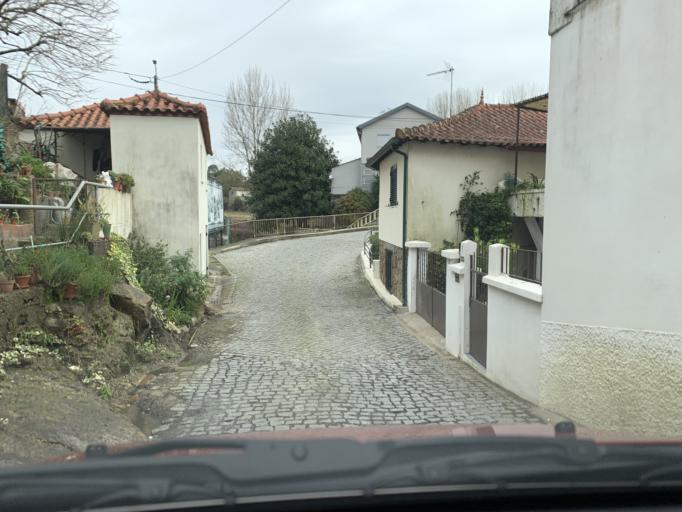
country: PT
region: Braga
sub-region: Vila Nova de Famalicao
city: Vila Nova de Famalicao
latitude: 41.4209
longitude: -8.5034
